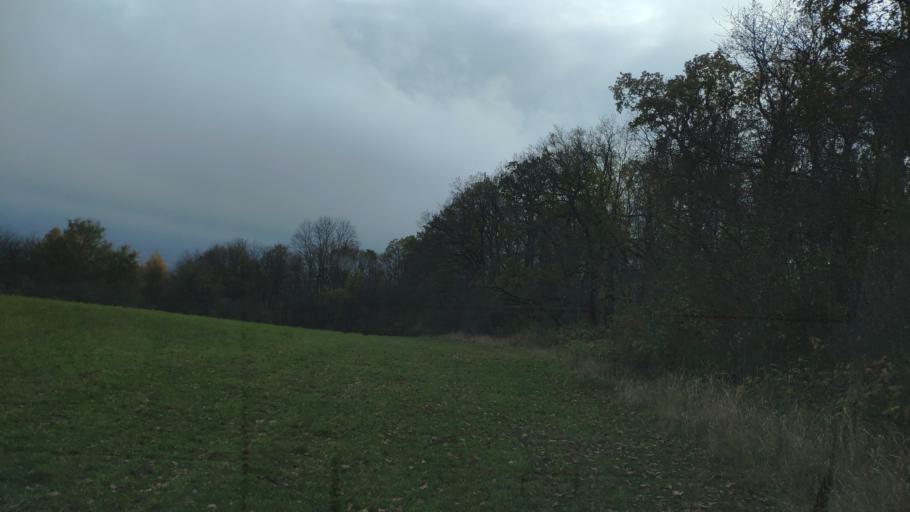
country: SK
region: Presovsky
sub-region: Okres Presov
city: Presov
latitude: 49.0039
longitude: 21.2006
